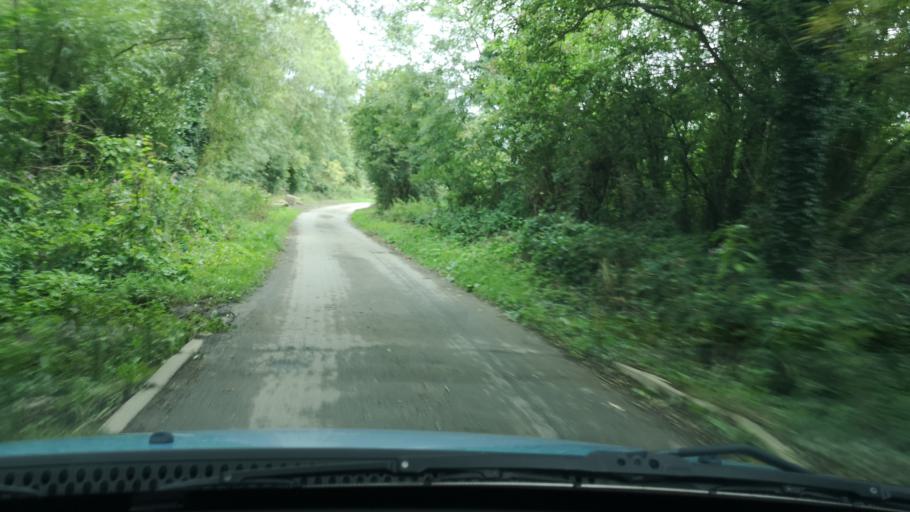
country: GB
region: England
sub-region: City and Borough of Wakefield
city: Featherstone
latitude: 53.6497
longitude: -1.3548
